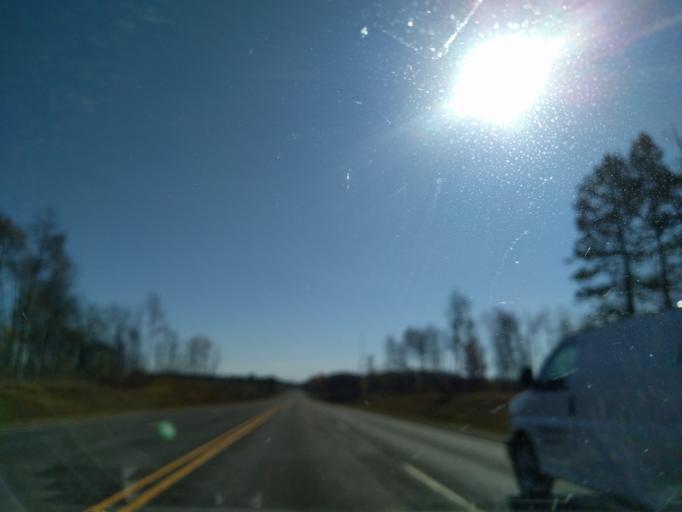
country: US
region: Michigan
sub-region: Iron County
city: Crystal Falls
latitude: 46.2328
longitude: -88.0077
